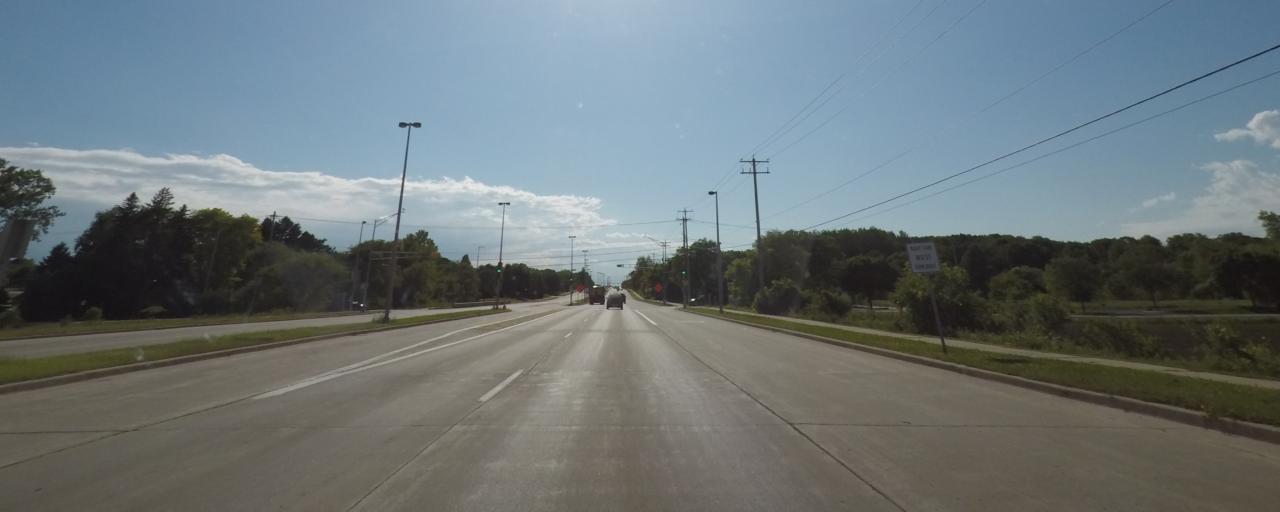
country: US
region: Wisconsin
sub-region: Milwaukee County
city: Greendale
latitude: 42.9160
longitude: -87.9980
